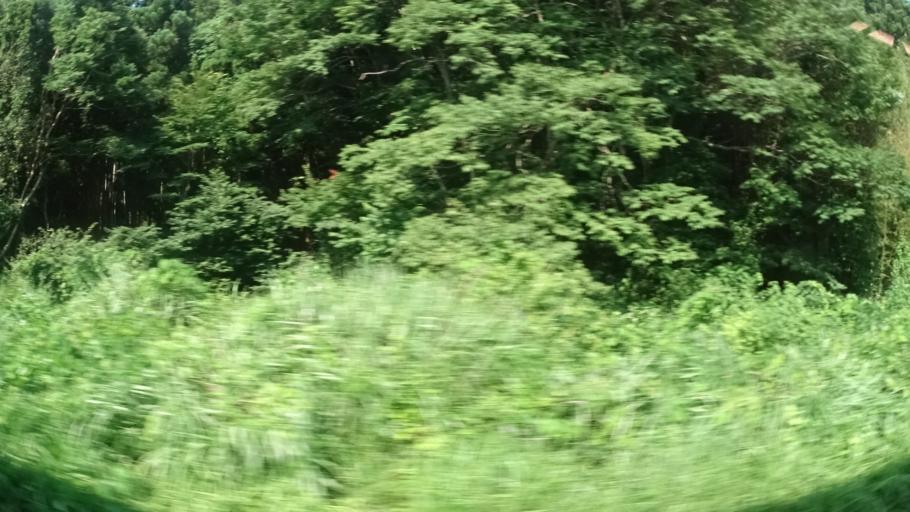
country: JP
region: Fukushima
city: Iwaki
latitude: 37.1666
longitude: 140.9985
